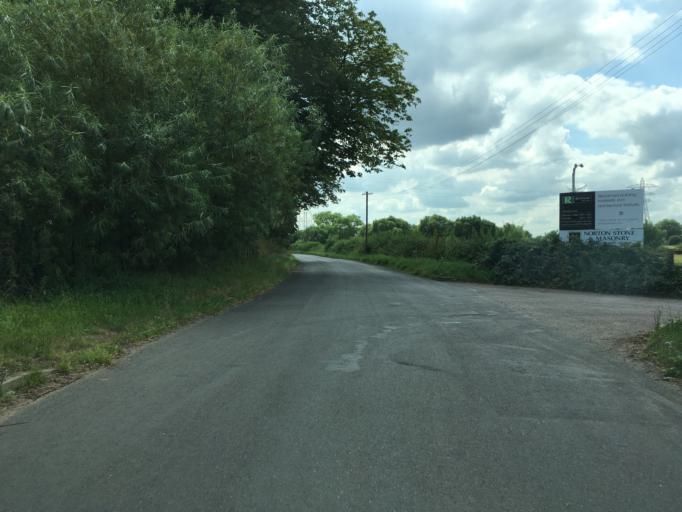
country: GB
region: England
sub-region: Gloucestershire
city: Gloucester
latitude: 51.8905
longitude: -2.2534
